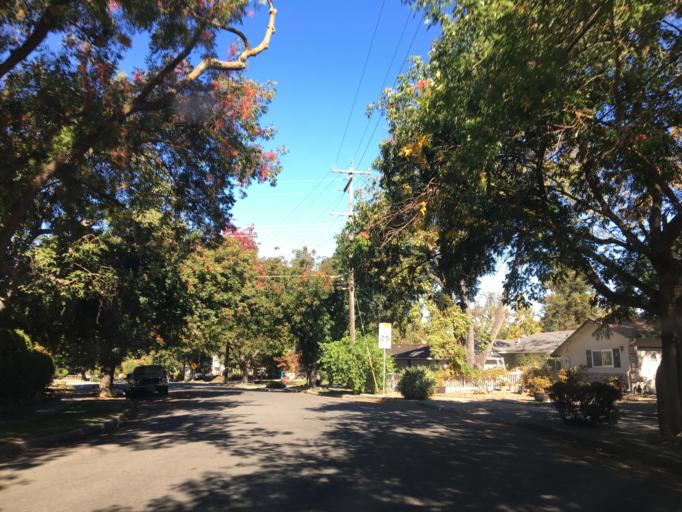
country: US
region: California
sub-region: Santa Clara County
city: San Jose
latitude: 37.3041
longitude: -121.8829
